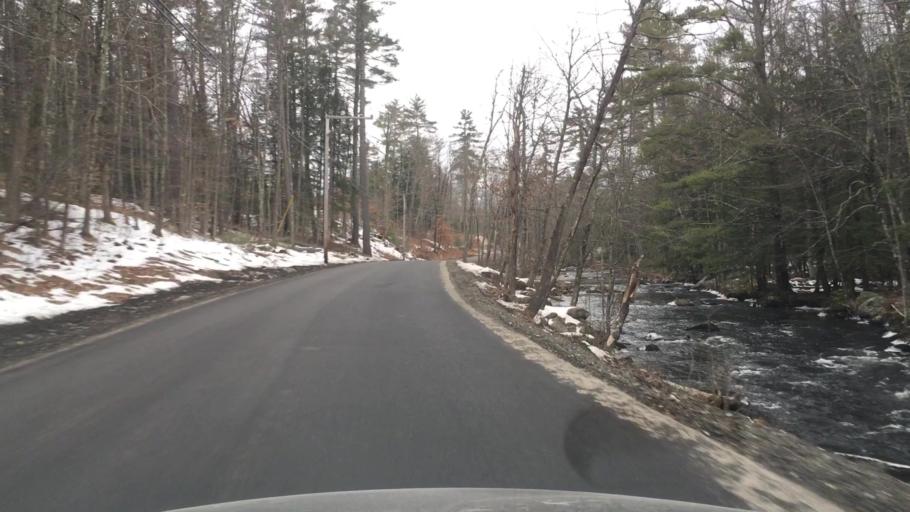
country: US
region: New Hampshire
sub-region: Hillsborough County
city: New Boston
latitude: 43.0035
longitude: -71.6635
